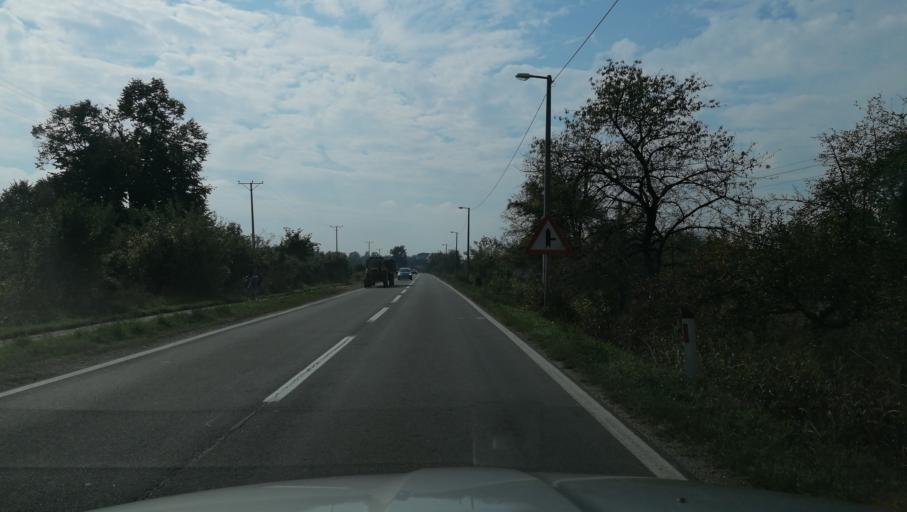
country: BA
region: Republika Srpska
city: Balatun
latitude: 44.8561
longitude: 19.3188
